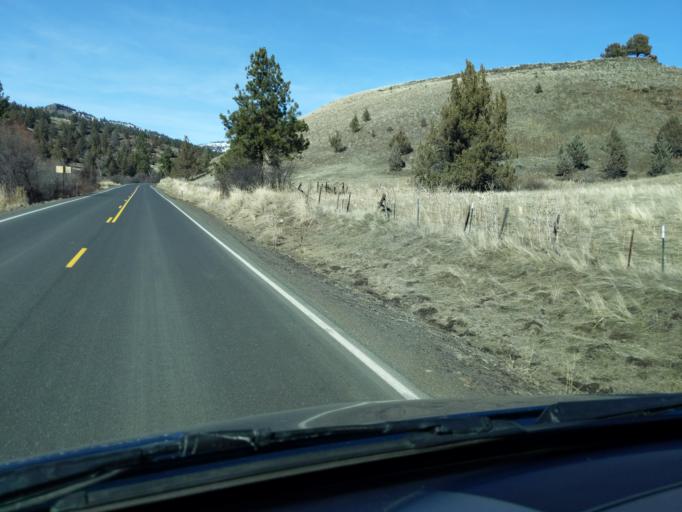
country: US
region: Oregon
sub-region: Grant County
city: John Day
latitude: 44.8416
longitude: -119.0314
